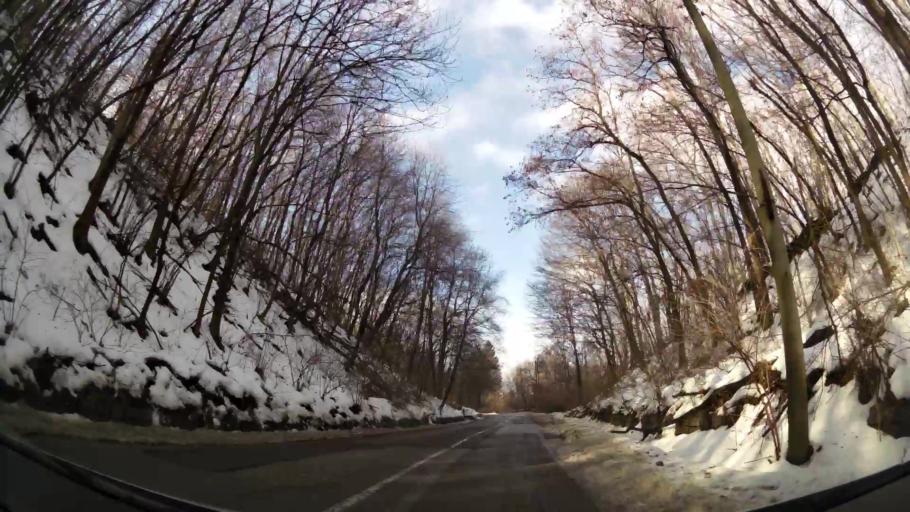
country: BG
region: Sofia-Capital
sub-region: Stolichna Obshtina
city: Sofia
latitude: 42.6455
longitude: 23.2493
